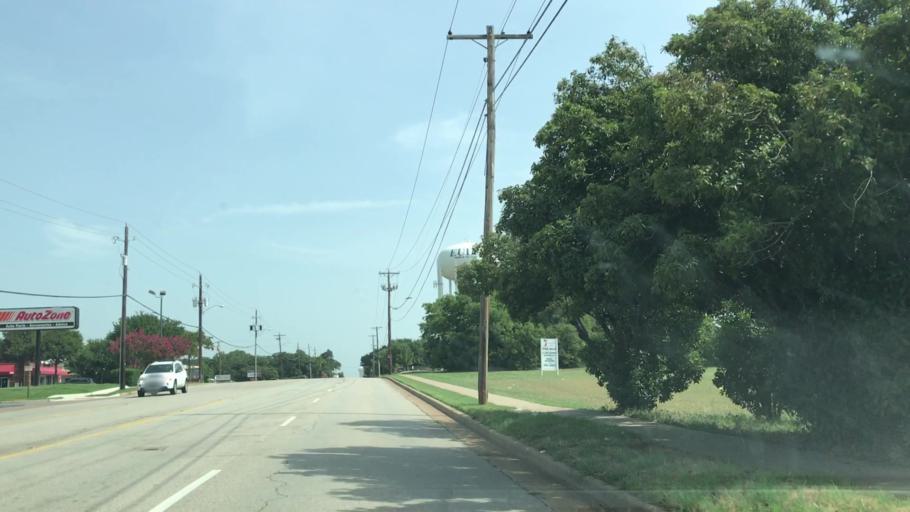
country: US
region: Texas
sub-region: Tarrant County
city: Euless
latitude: 32.8536
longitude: -97.0824
